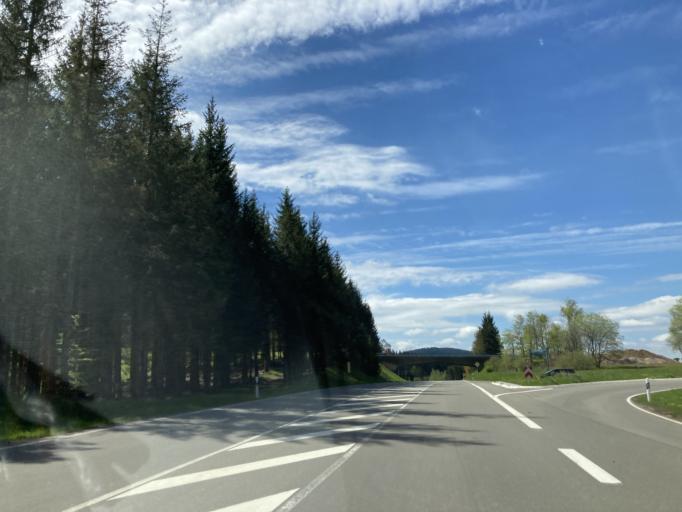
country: DE
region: Baden-Wuerttemberg
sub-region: Freiburg Region
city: Gutenbach
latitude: 48.0277
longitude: 8.1788
